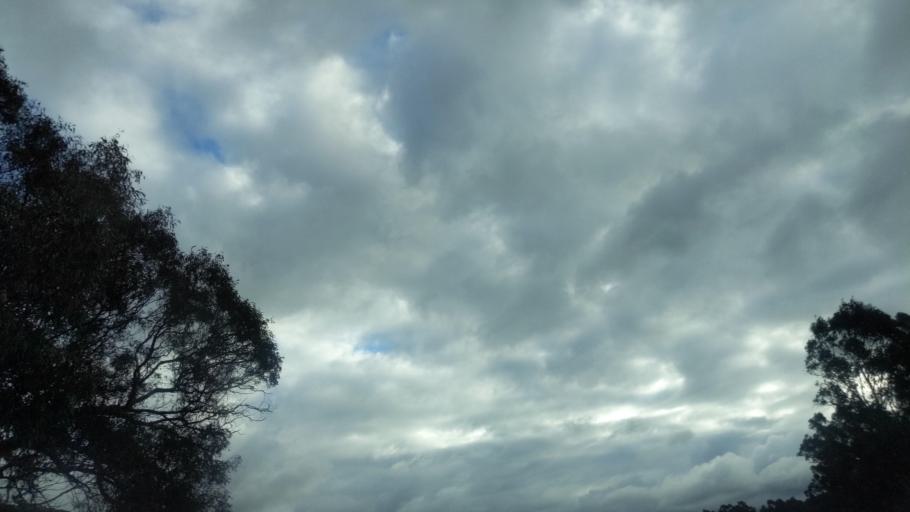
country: AU
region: New South Wales
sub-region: Wagga Wagga
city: Forest Hill
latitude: -35.1614
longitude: 147.5094
